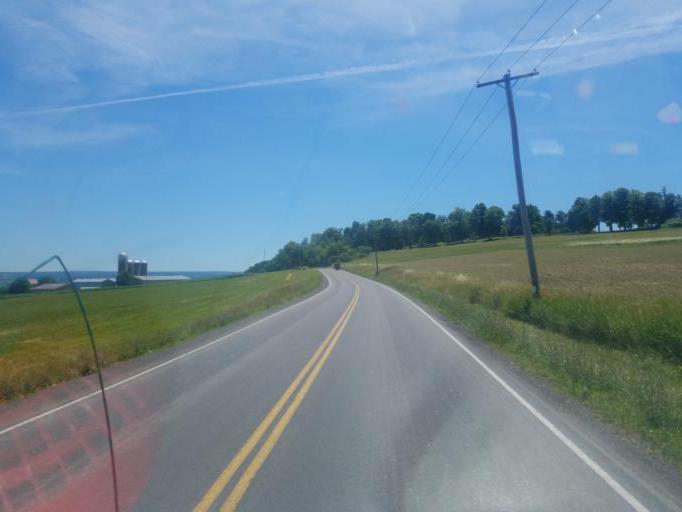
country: US
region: New York
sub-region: Yates County
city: Dundee
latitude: 42.6009
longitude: -76.9674
